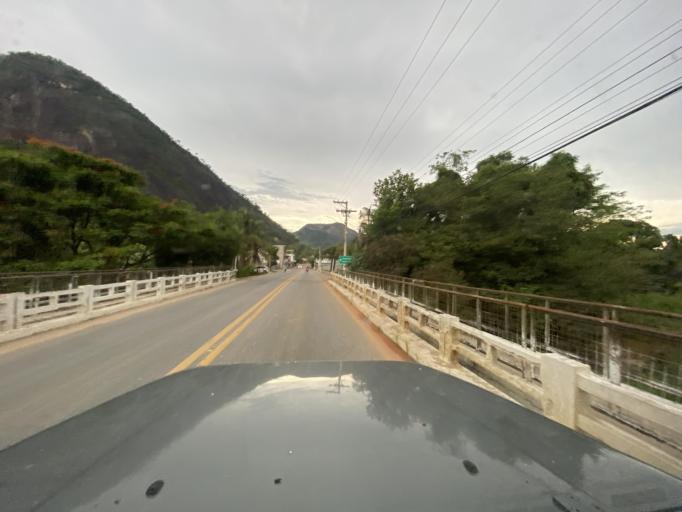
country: BR
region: Espirito Santo
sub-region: Jeronimo Monteiro
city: Jeronimo Monteiro
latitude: -20.7946
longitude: -41.3773
